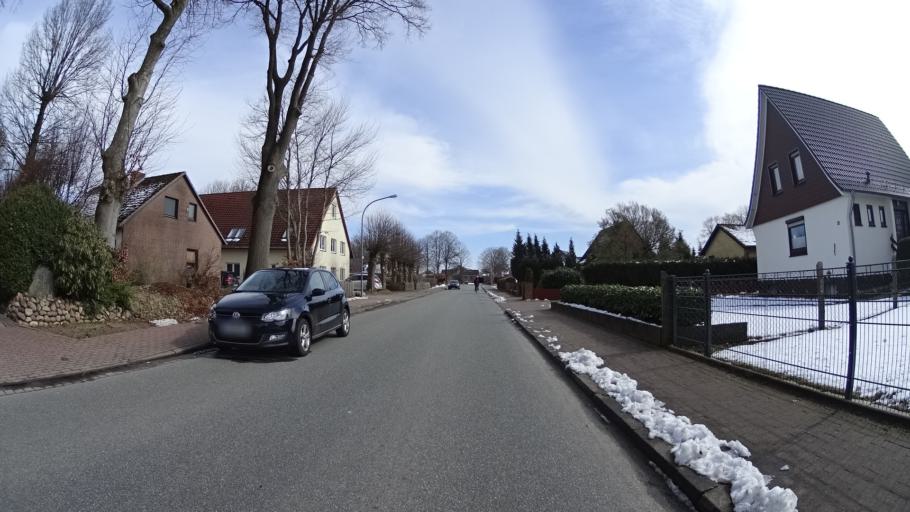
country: DE
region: Schleswig-Holstein
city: Gross Kummerfeld
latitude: 54.0270
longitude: 10.1108
